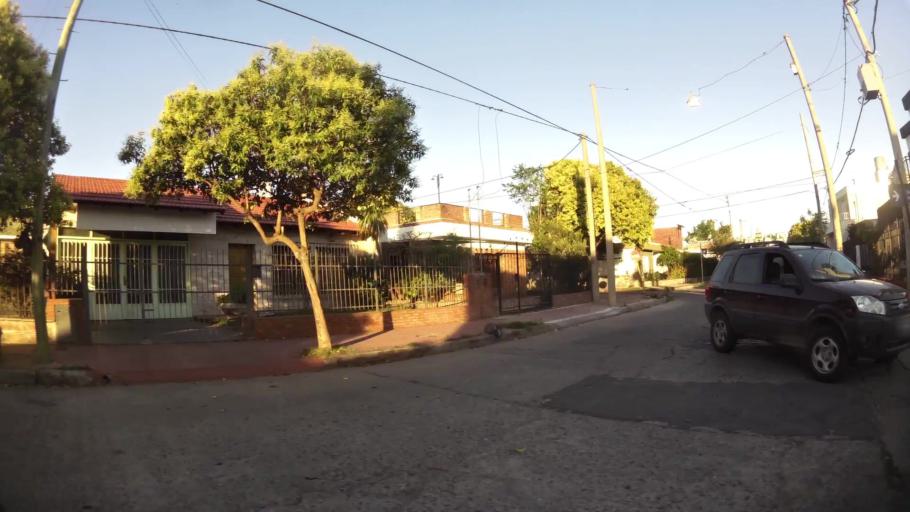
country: AR
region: Cordoba
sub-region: Departamento de Capital
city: Cordoba
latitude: -31.3897
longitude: -64.2111
